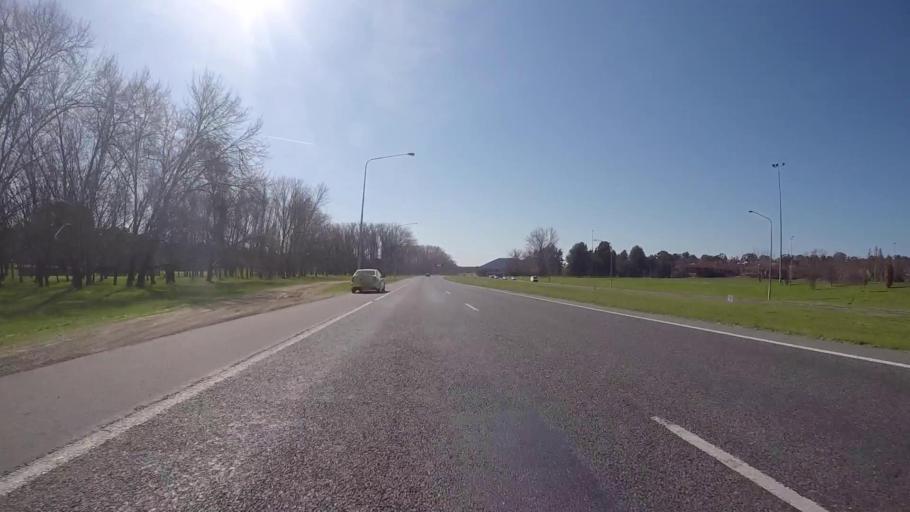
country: AU
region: Australian Capital Territory
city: Forrest
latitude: -35.3333
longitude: 149.0861
